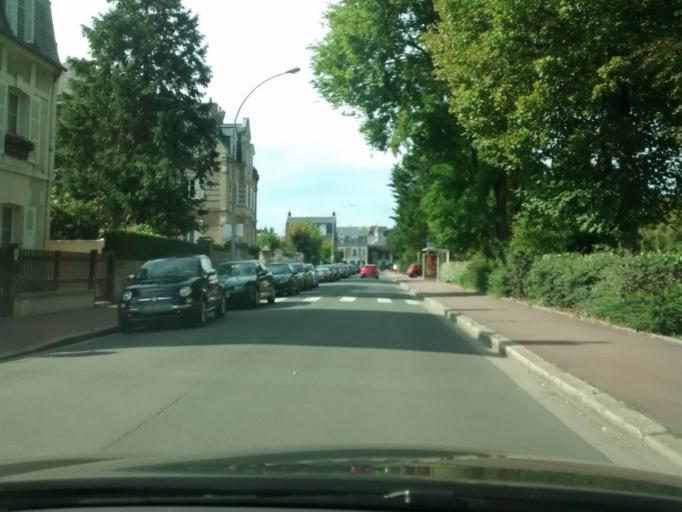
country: FR
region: Lower Normandy
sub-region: Departement du Calvados
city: Deauville
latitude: 49.3542
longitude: 0.0705
